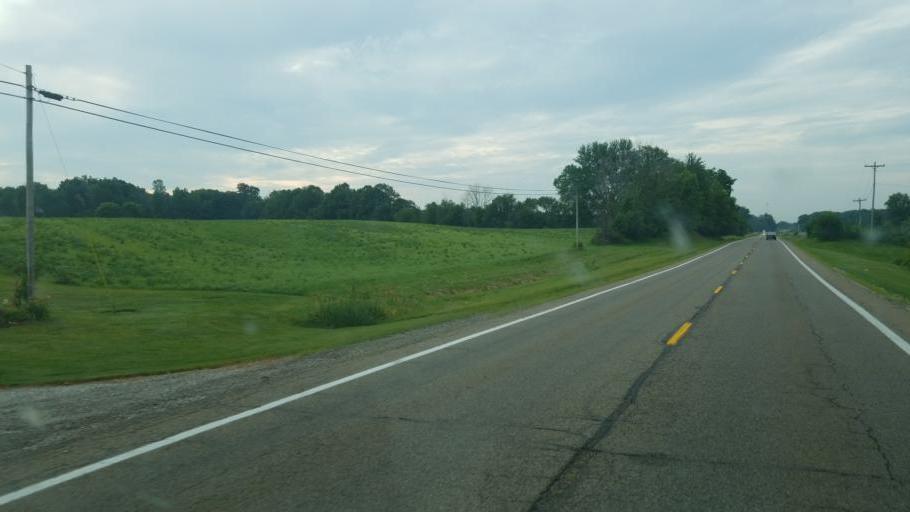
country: US
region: Ohio
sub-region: Morrow County
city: Mount Gilead
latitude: 40.5133
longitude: -82.7417
